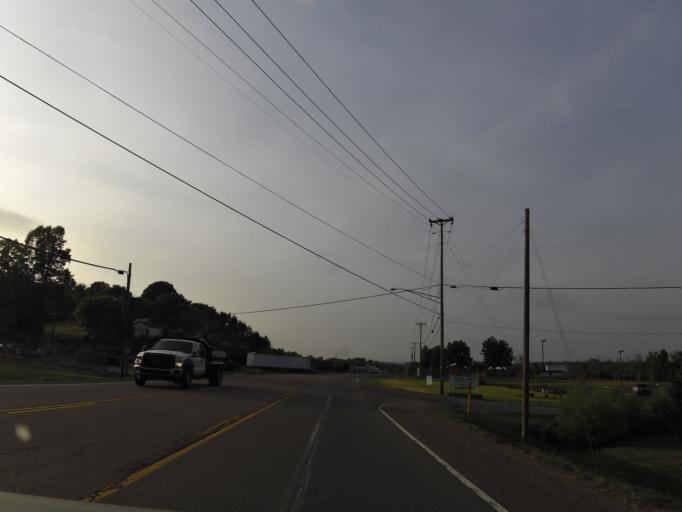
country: US
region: Tennessee
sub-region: Knox County
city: Knoxville
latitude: 35.9670
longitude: -83.8273
